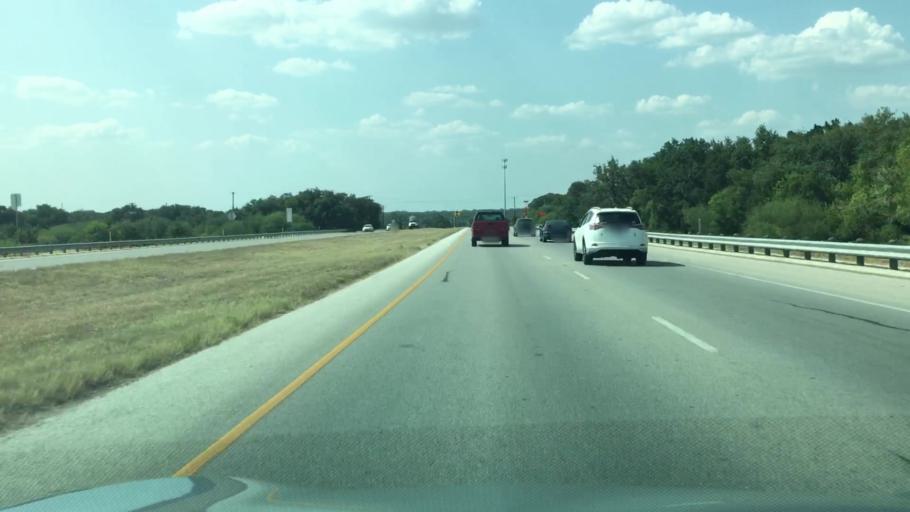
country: US
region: Texas
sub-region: Hays County
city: San Marcos
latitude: 29.8764
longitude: -97.9683
